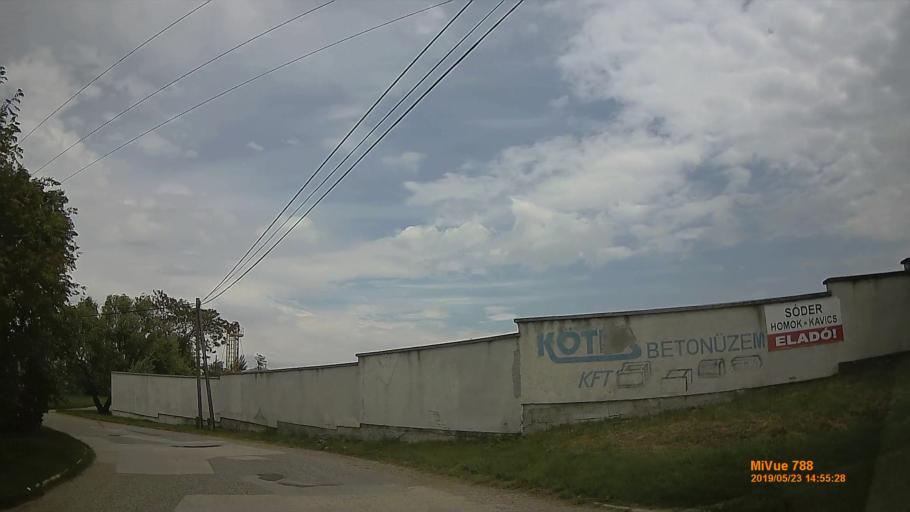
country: HU
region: Veszprem
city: Veszprem
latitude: 47.1205
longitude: 17.9550
